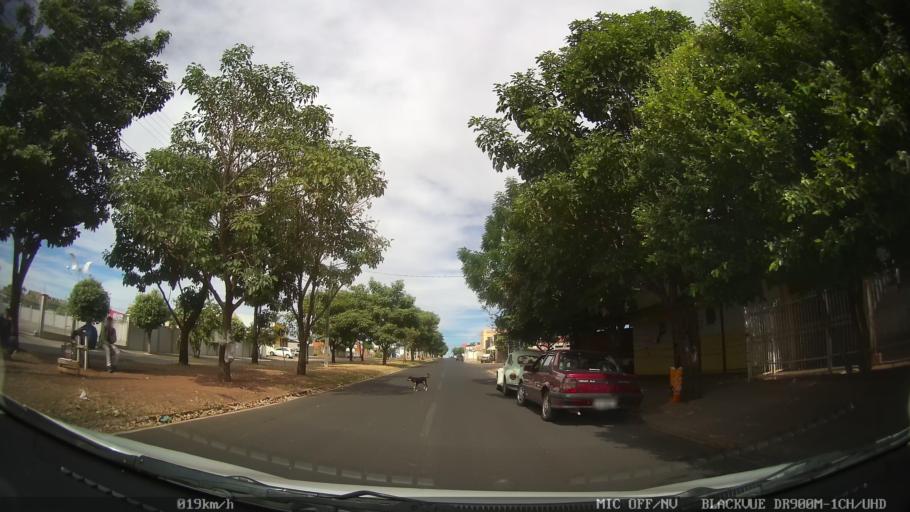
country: BR
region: Sao Paulo
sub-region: Catanduva
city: Catanduva
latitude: -21.1643
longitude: -48.9700
